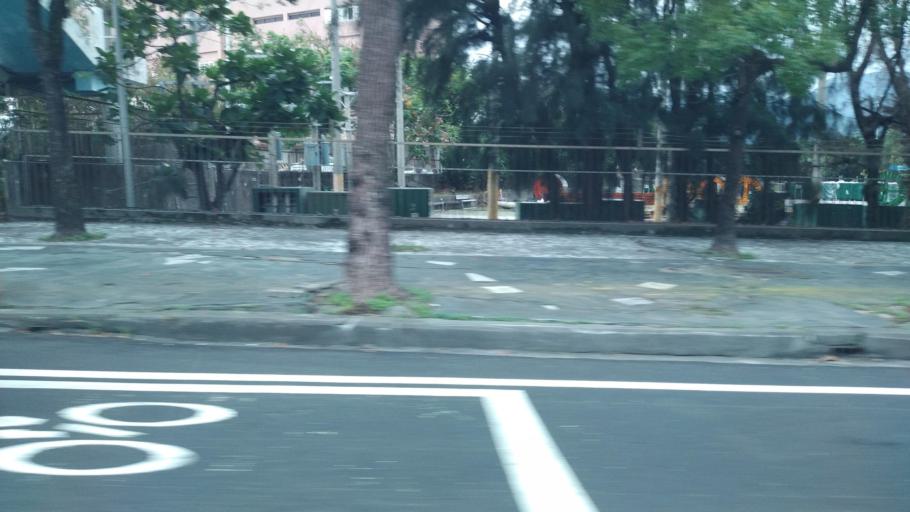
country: TW
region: Taiwan
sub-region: Hualien
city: Hualian
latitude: 24.0065
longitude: 121.6181
